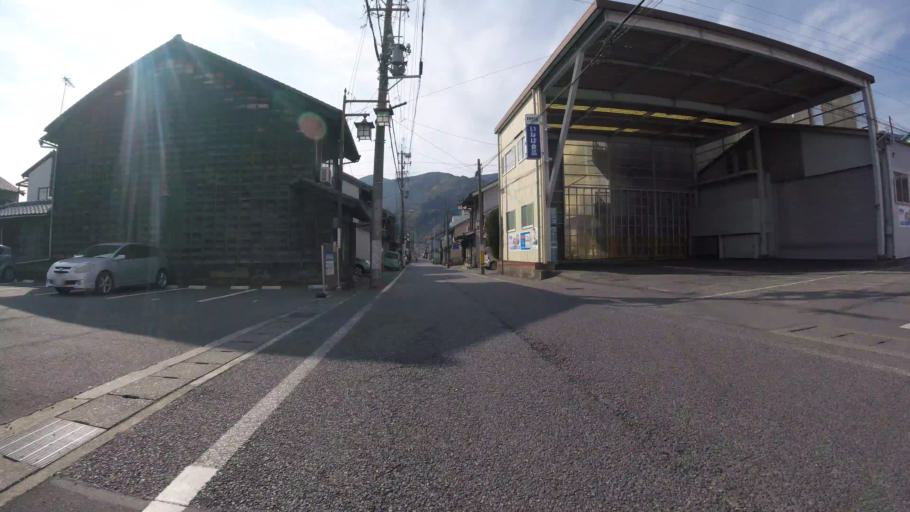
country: JP
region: Shizuoka
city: Fujinomiya
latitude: 35.1047
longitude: 138.5615
